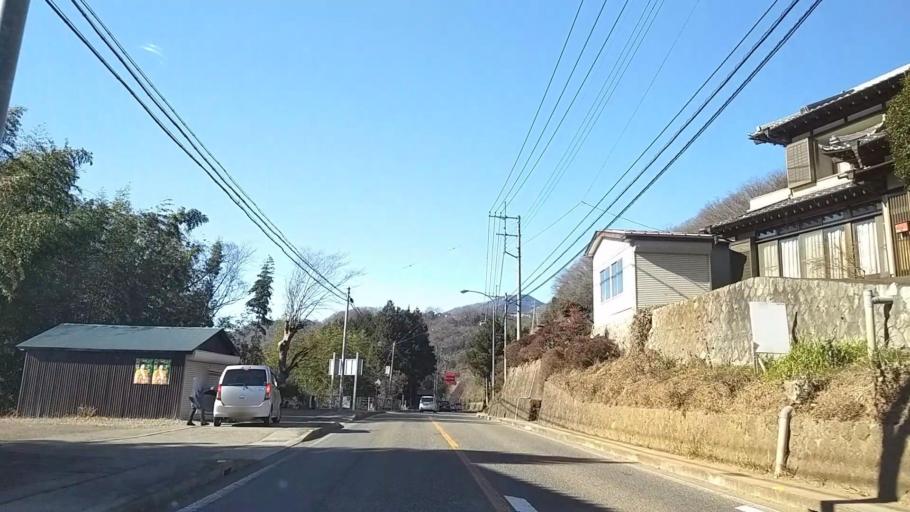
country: JP
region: Yamanashi
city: Uenohara
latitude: 35.6134
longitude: 139.0805
